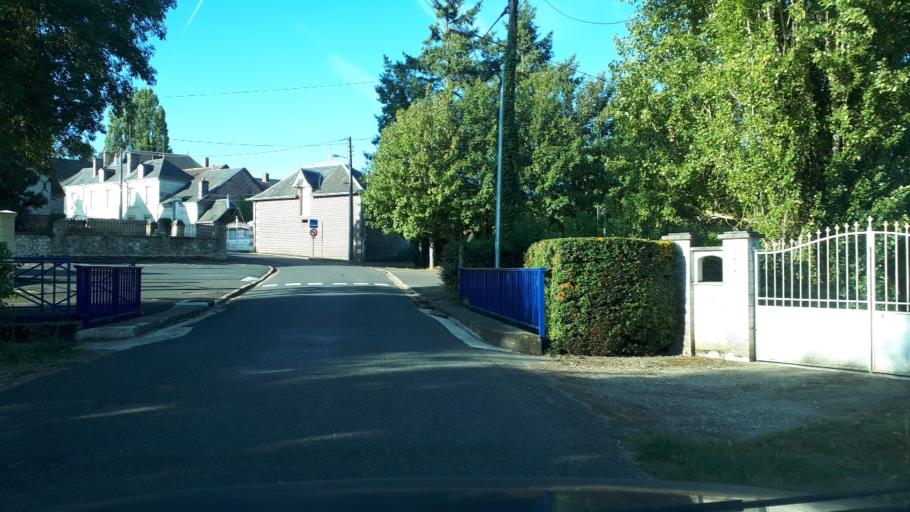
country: FR
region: Centre
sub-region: Departement du Loir-et-Cher
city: Montoire-sur-le-Loir
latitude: 47.6964
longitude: 0.9228
